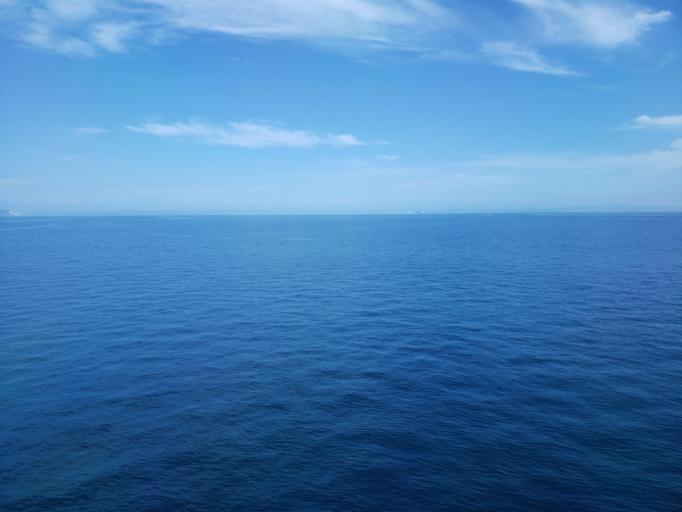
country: JP
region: Hyogo
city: Shirahamacho-usazakiminami
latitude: 34.5528
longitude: 134.7438
